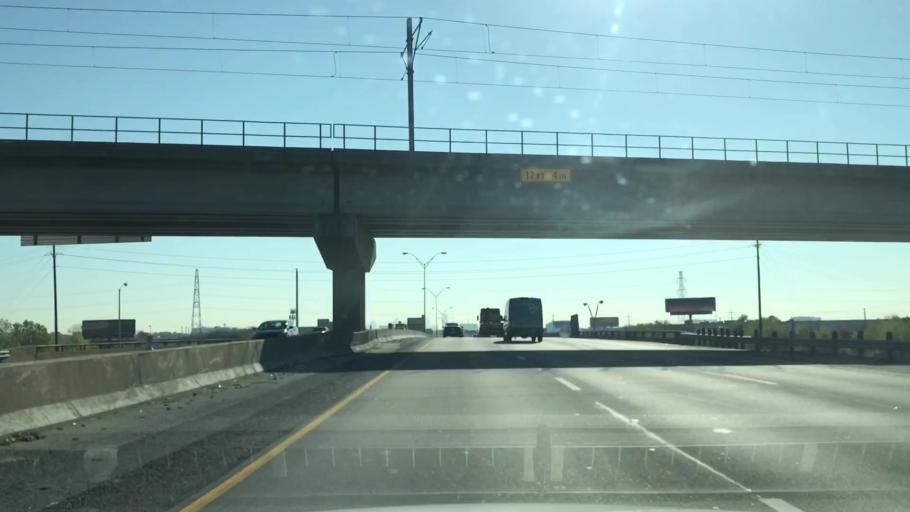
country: US
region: Texas
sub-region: Dallas County
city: Farmers Branch
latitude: 32.8545
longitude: -96.8859
